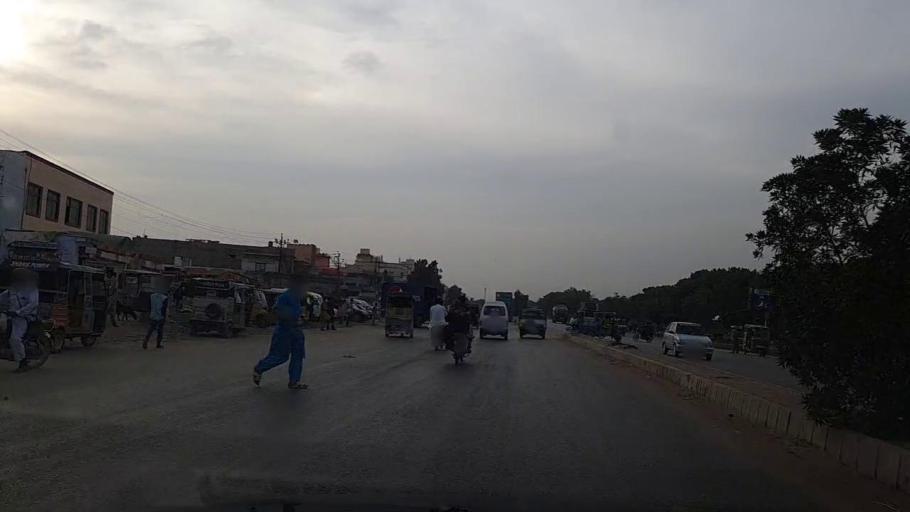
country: PK
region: Sindh
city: Malir Cantonment
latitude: 24.8598
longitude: 67.3366
